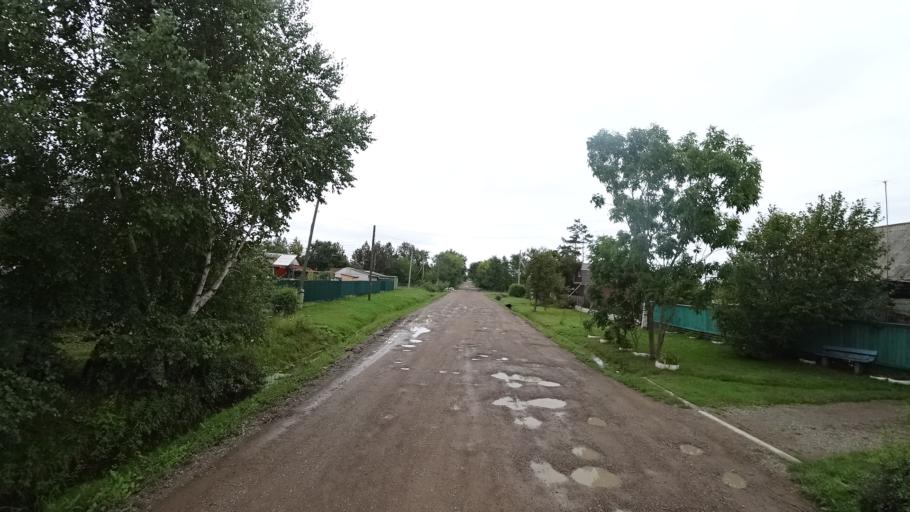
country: RU
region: Primorskiy
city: Chernigovka
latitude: 44.3422
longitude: 132.5653
